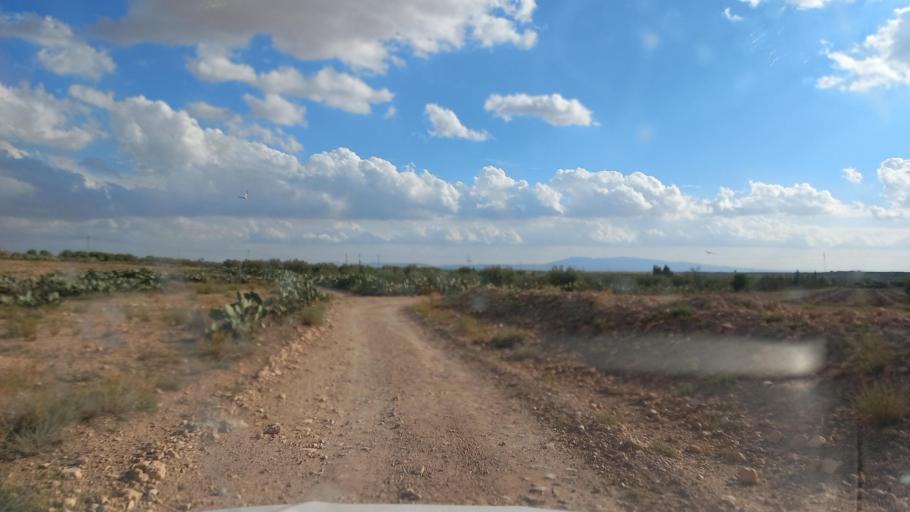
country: TN
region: Al Qasrayn
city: Sbiba
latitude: 35.3876
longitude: 9.0400
